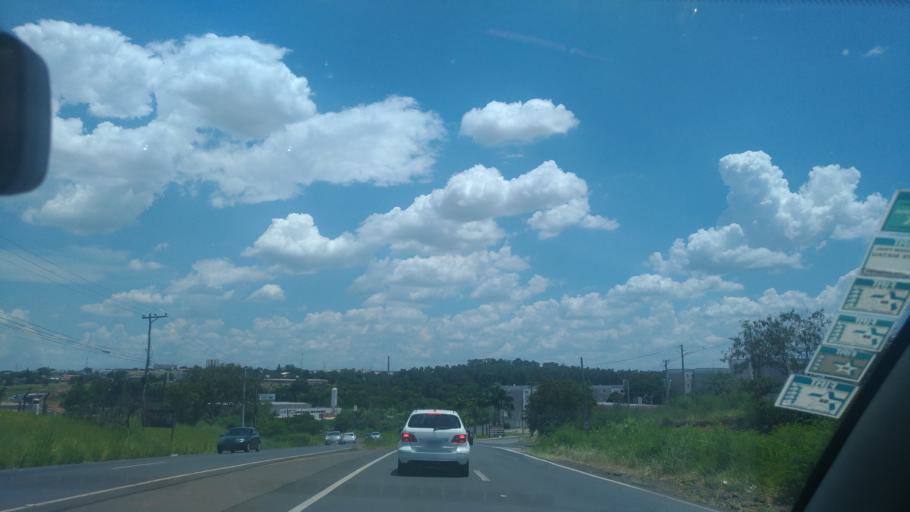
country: BR
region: Sao Paulo
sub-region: Americana
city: Americana
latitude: -22.7603
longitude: -47.3206
